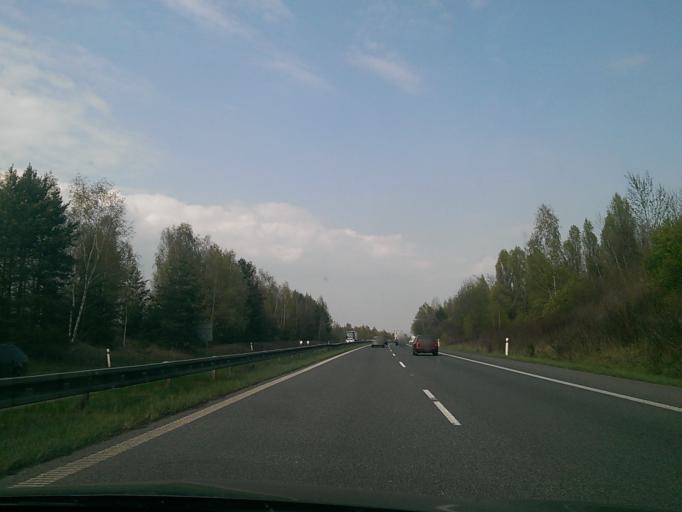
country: CZ
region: Central Bohemia
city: Mnichovo Hradiste
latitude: 50.5113
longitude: 14.9826
